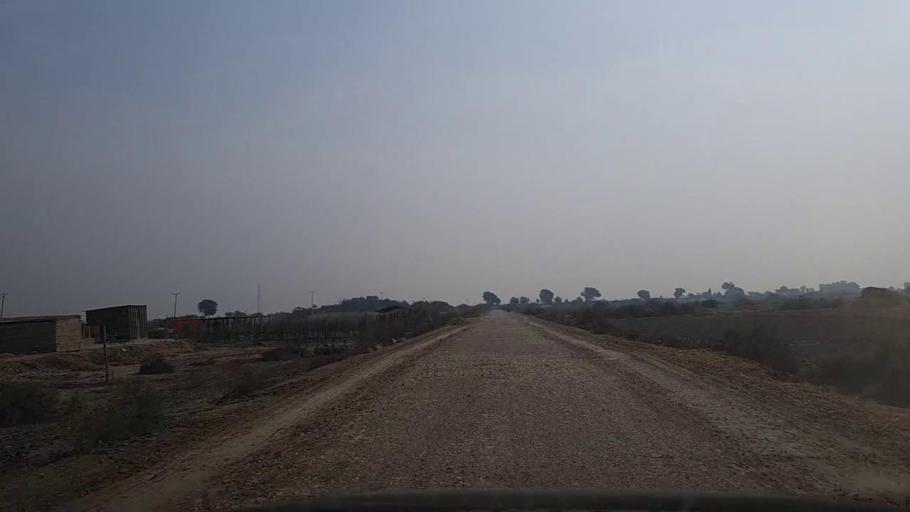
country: PK
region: Sindh
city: Mirpur Sakro
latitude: 24.3789
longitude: 67.7548
